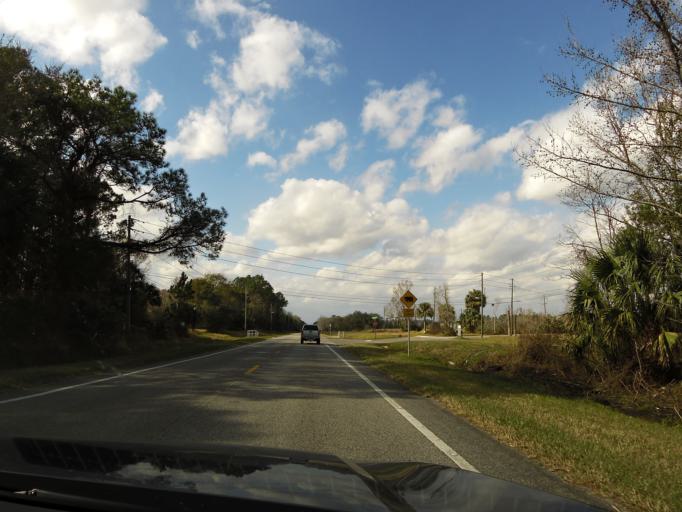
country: US
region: Florida
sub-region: Volusia County
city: De Leon Springs
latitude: 29.1581
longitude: -81.3838
